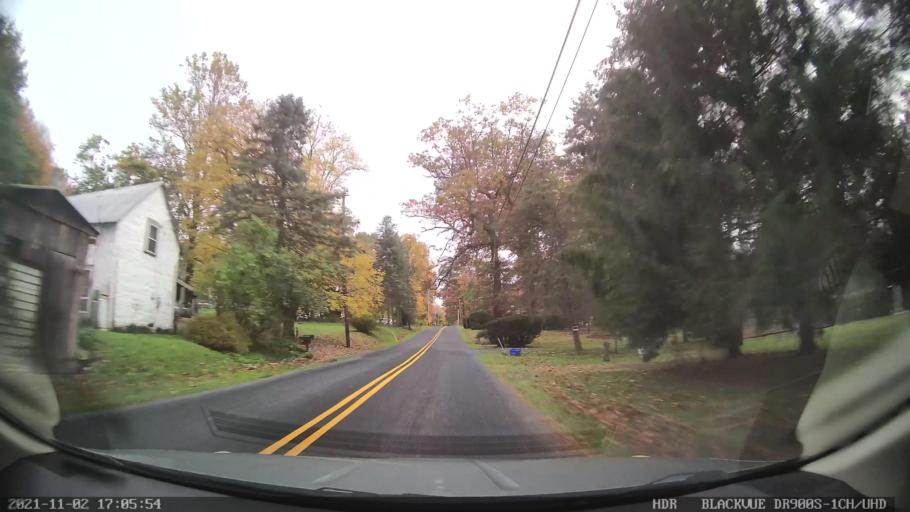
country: US
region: Pennsylvania
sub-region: Berks County
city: Fleetwood
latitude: 40.4252
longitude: -75.8409
